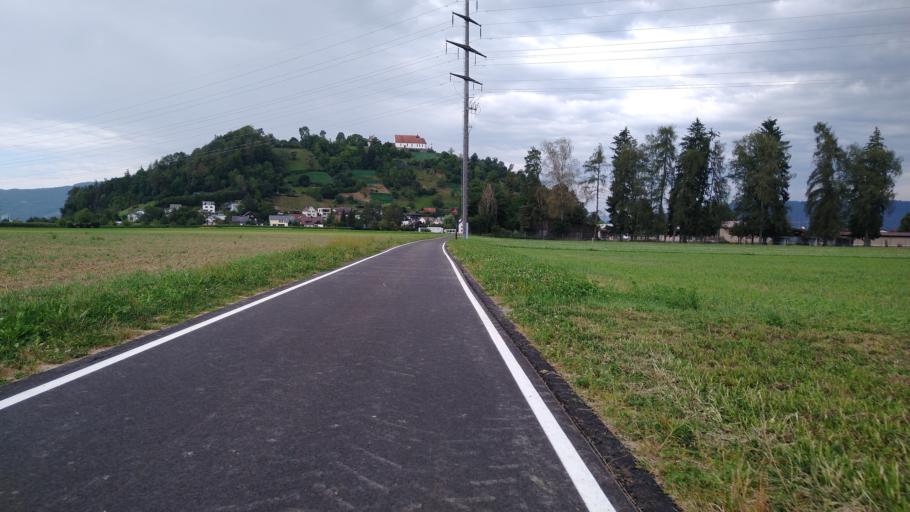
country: CH
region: Aargau
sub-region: Bezirk Lenzburg
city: Staufen
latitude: 47.3735
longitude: 8.1652
